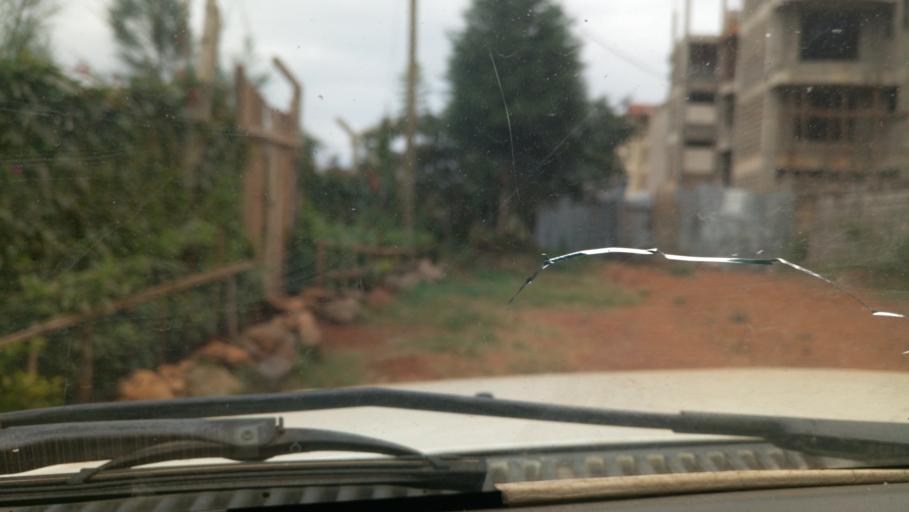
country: KE
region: Nairobi Area
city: Pumwani
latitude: -1.2297
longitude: 36.8765
